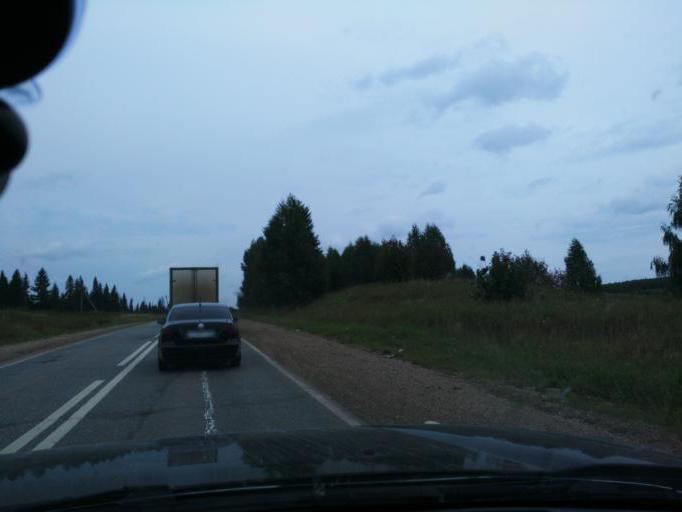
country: RU
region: Bashkortostan
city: Verkhniye Tatyshly
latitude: 56.4949
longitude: 55.8242
